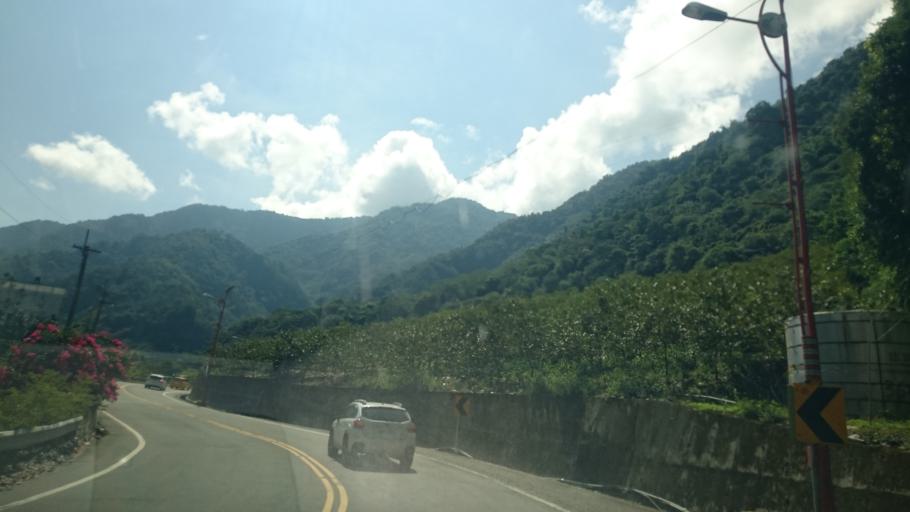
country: TW
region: Taiwan
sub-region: Nantou
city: Puli
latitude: 23.9953
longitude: 121.0713
